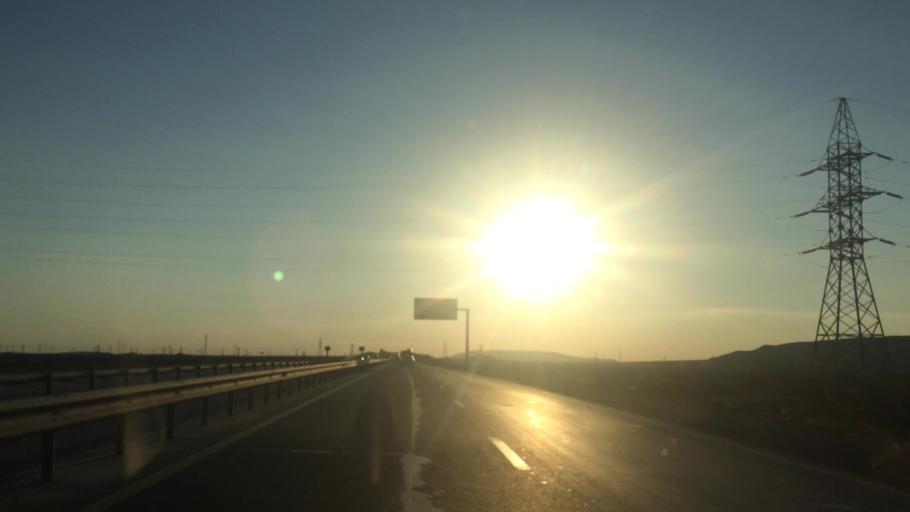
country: AZ
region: Baki
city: Qobustan
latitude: 39.9626
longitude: 49.3985
